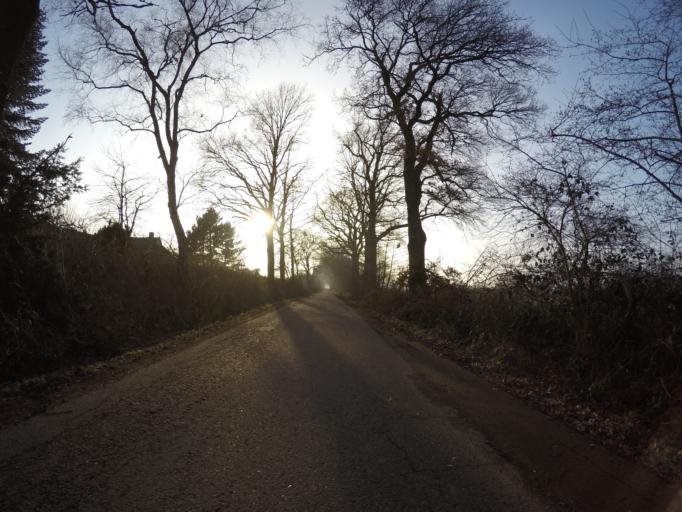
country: DE
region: Schleswig-Holstein
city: Quickborn
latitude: 53.7089
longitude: 9.8917
